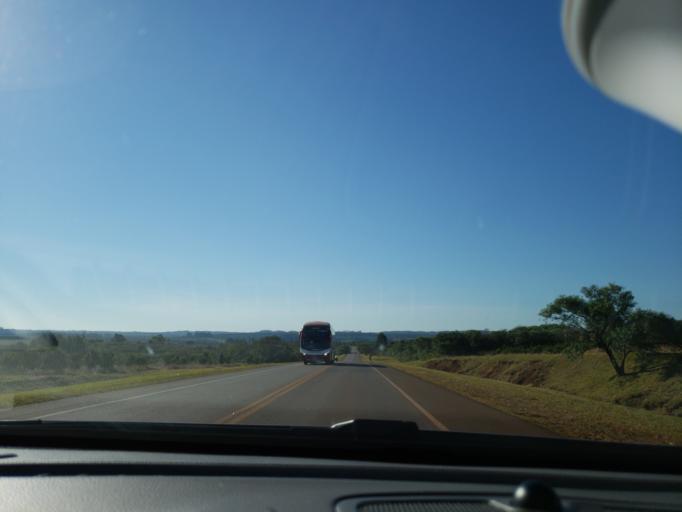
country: AR
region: Misiones
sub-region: Departamento de Apostoles
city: Apostoles
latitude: -27.8616
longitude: -55.7645
